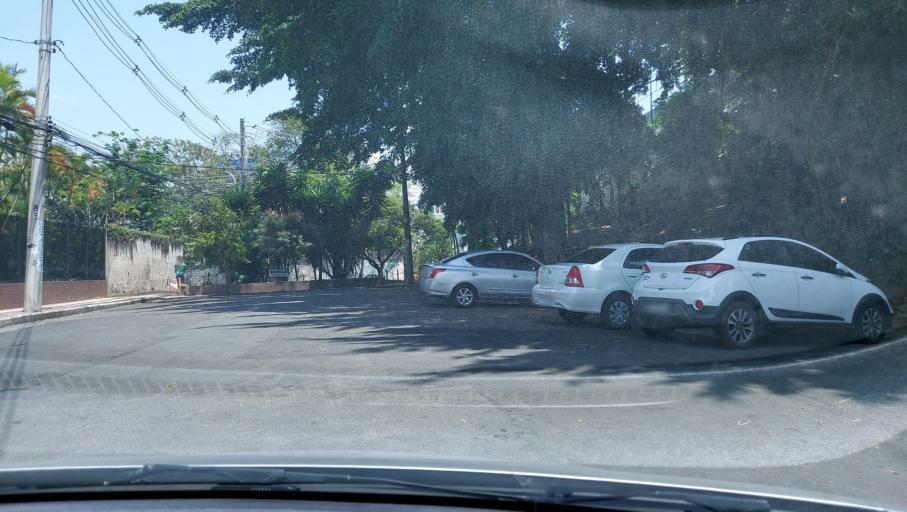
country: BR
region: Bahia
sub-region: Salvador
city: Salvador
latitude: -12.9846
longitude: -38.4632
